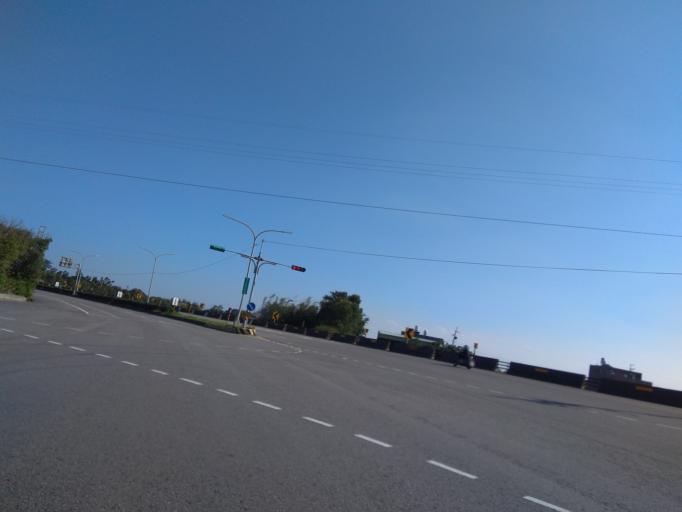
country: TW
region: Taiwan
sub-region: Hsinchu
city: Zhubei
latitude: 25.0237
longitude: 121.0823
